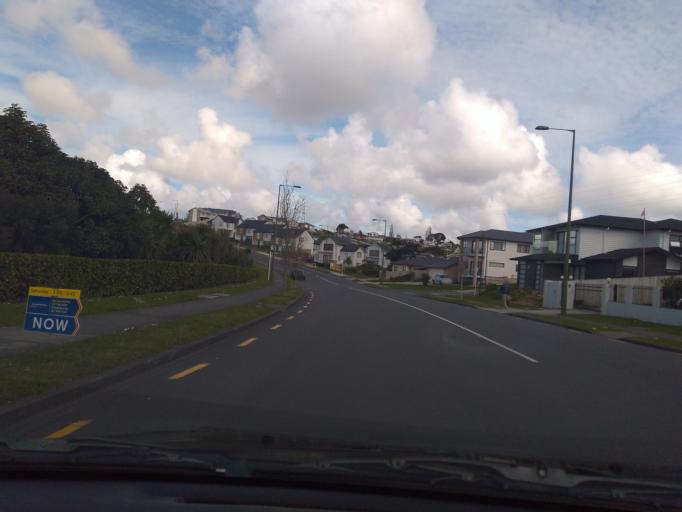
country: NZ
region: Auckland
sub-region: Auckland
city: Rosebank
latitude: -36.8260
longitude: 174.6152
